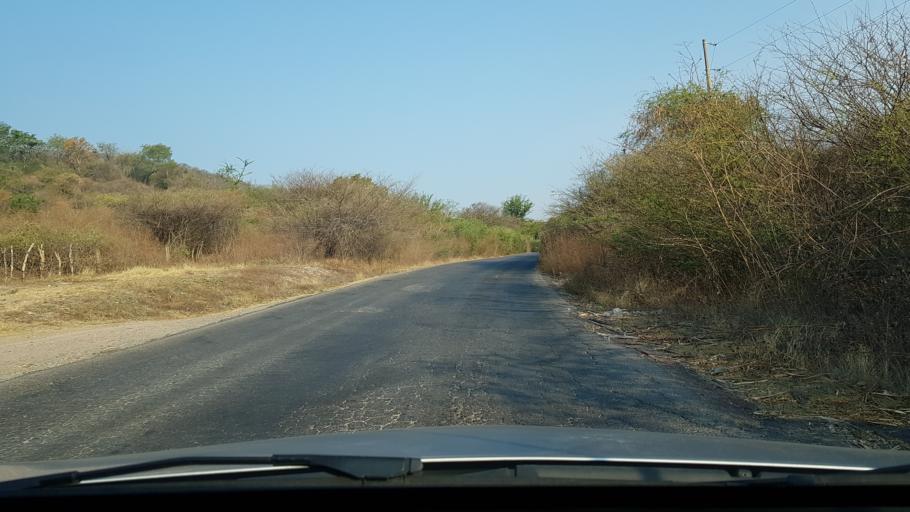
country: MX
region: Morelos
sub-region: Tepalcingo
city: Zacapalco
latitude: 18.6489
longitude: -99.0279
